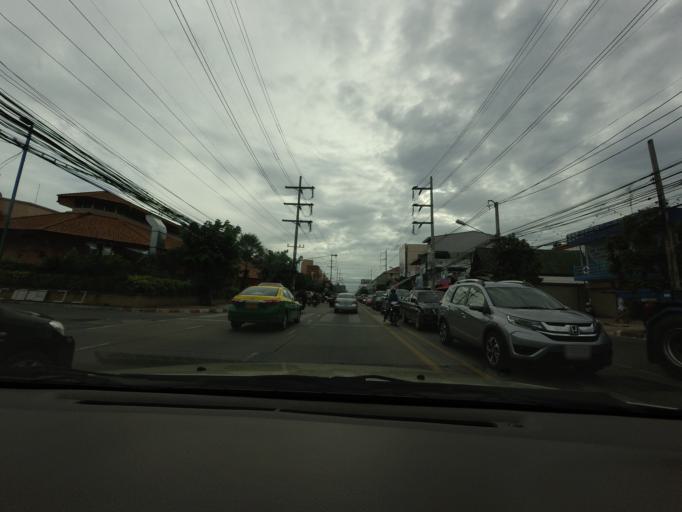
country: TH
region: Chon Buri
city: Phatthaya
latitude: 12.9091
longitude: 100.8955
